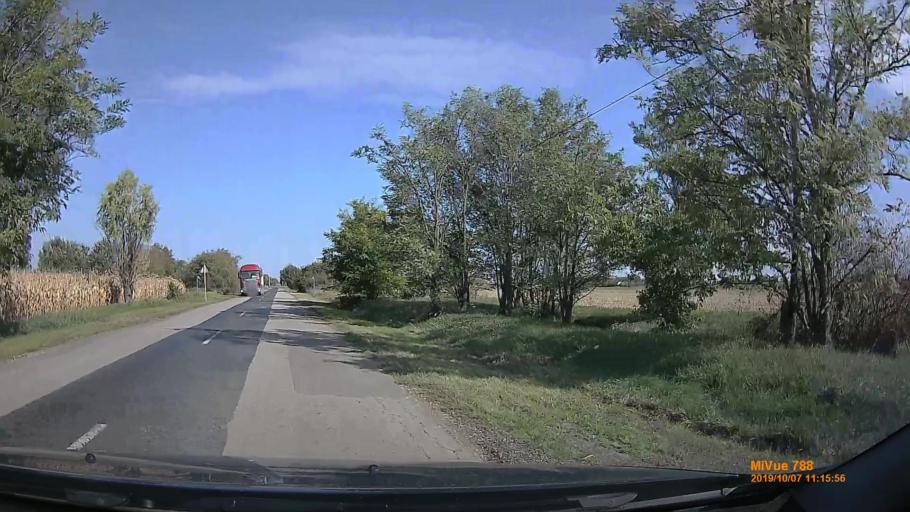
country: HU
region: Bekes
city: Kondoros
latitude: 46.7305
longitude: 20.7806
